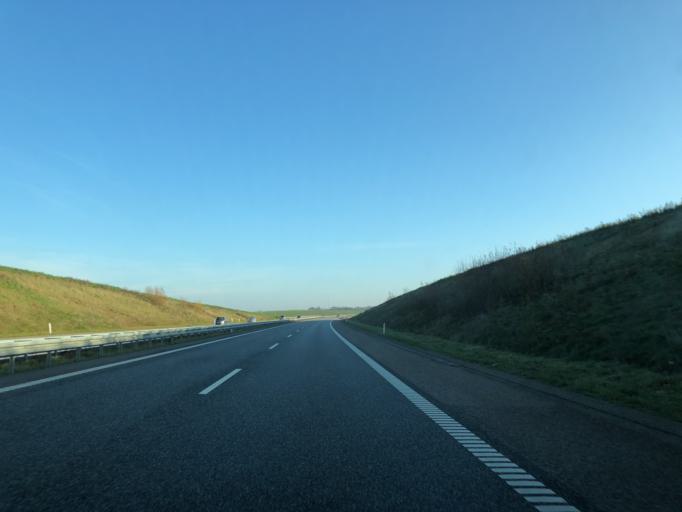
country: DK
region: Central Jutland
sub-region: Hedensted Kommune
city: Torring
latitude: 55.8325
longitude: 9.5043
